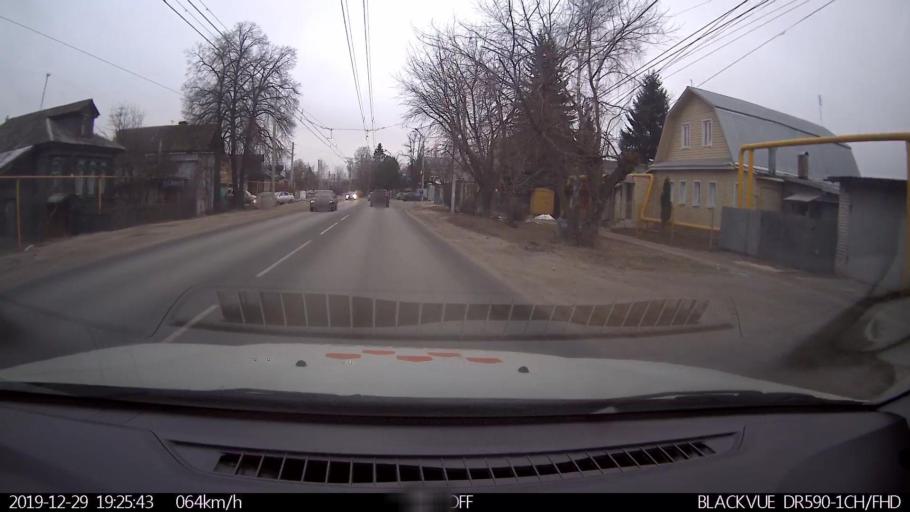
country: RU
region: Nizjnij Novgorod
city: Neklyudovo
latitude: 56.3742
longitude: 43.8358
